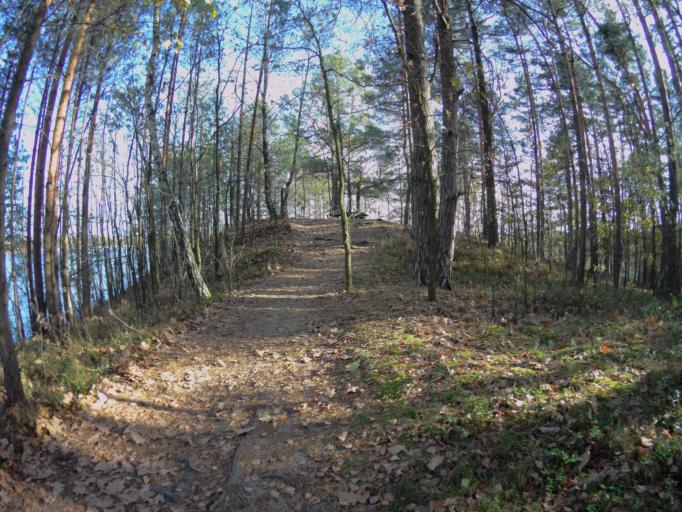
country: PL
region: Subcarpathian Voivodeship
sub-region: Powiat kolbuszowski
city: Lipnica
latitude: 50.3387
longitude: 21.9299
